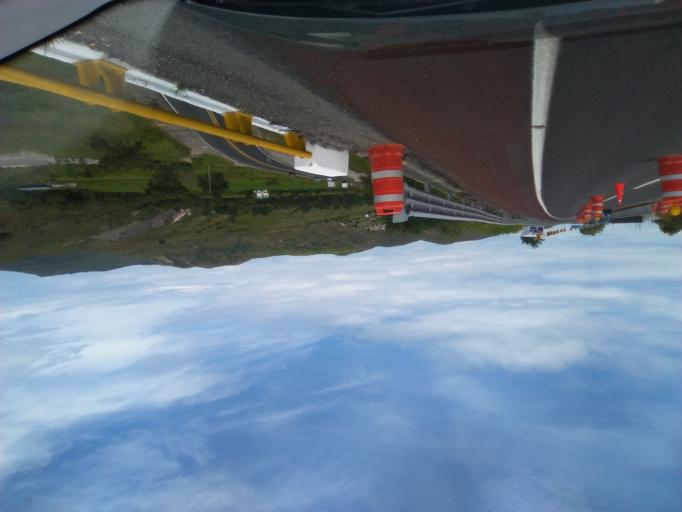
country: MX
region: Guerrero
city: Mazatlan
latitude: 17.4188
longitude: -99.4645
